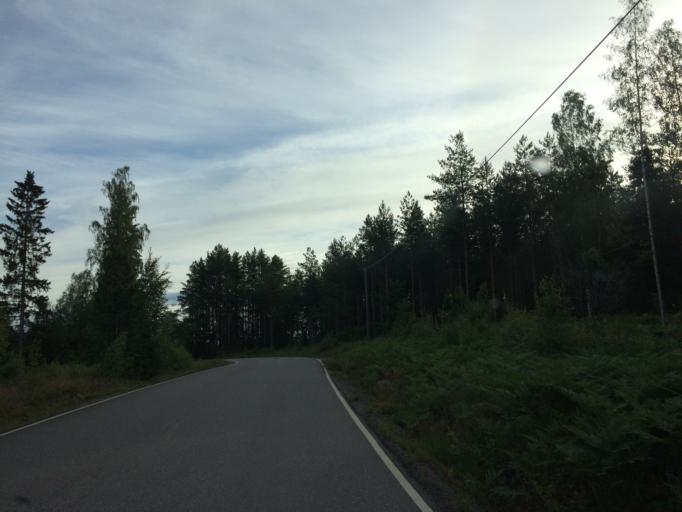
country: FI
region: Haeme
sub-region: Haemeenlinna
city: Janakkala
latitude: 60.8659
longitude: 24.5524
